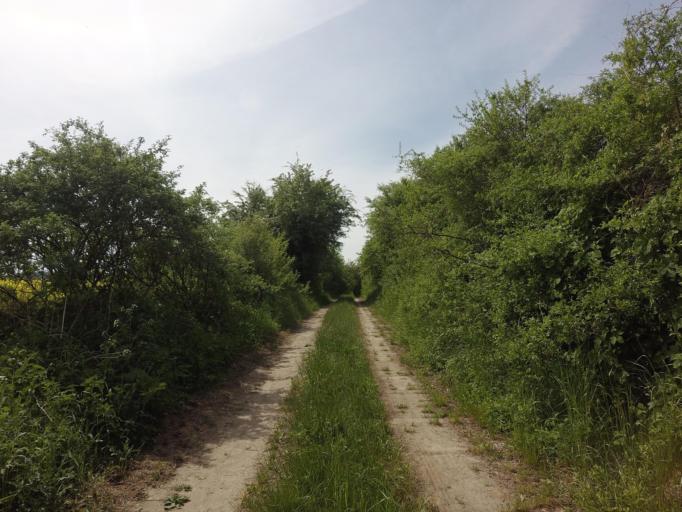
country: PL
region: West Pomeranian Voivodeship
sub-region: Powiat mysliborski
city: Barlinek
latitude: 53.0897
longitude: 15.2004
